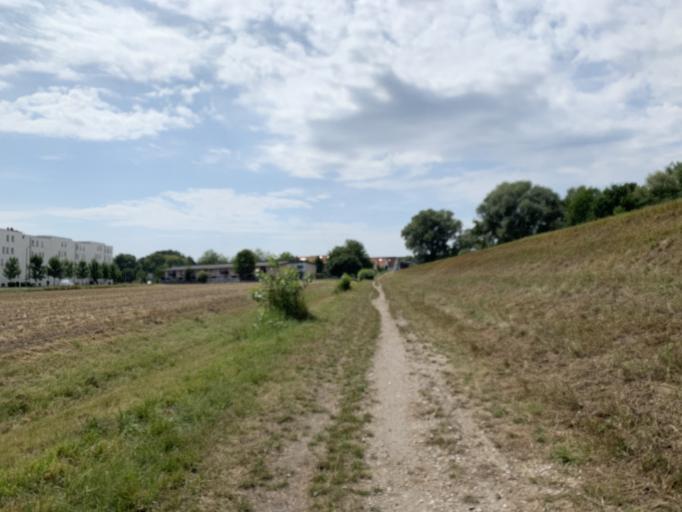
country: DE
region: Bavaria
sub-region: Upper Bavaria
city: Freising
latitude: 48.4002
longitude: 11.7630
